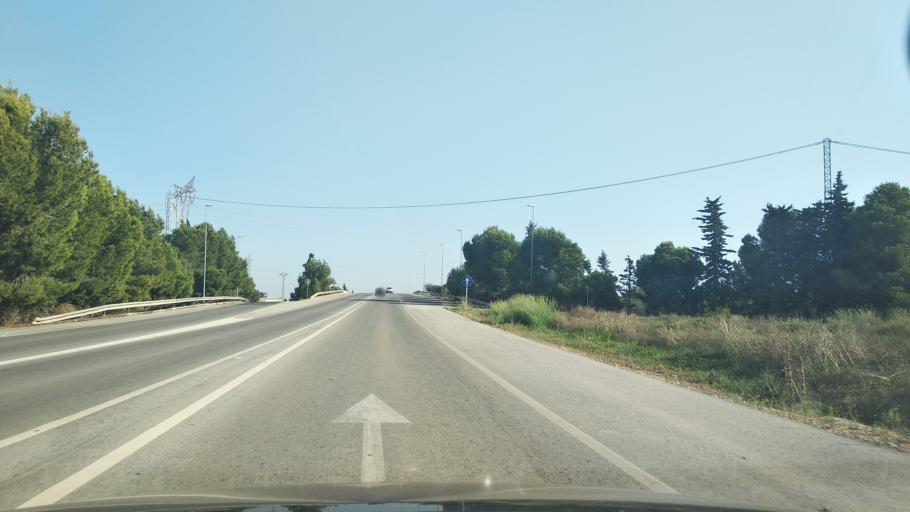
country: ES
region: Murcia
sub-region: Murcia
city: San Javier
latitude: 37.8170
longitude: -0.8445
